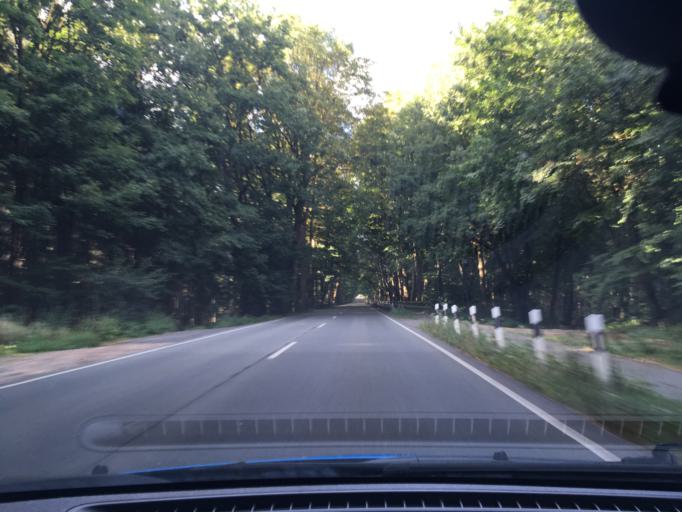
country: DE
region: Lower Saxony
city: Seevetal
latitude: 53.4154
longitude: 9.9280
